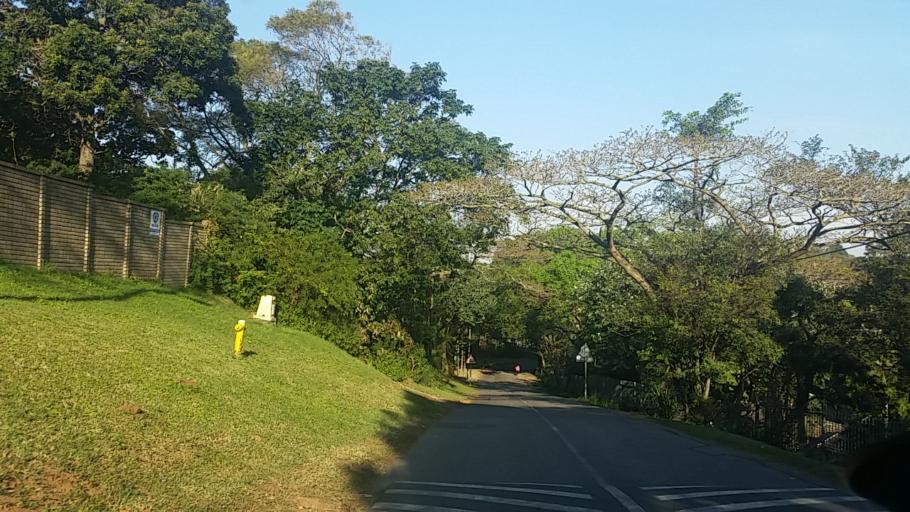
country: ZA
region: KwaZulu-Natal
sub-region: eThekwini Metropolitan Municipality
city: Berea
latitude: -29.8386
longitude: 30.9212
